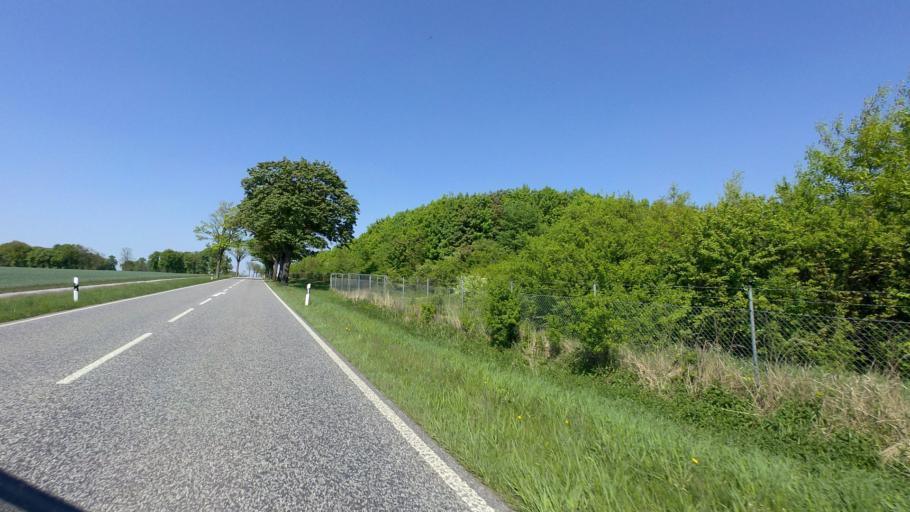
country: DE
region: Brandenburg
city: Beeskow
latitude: 52.1559
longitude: 14.2588
